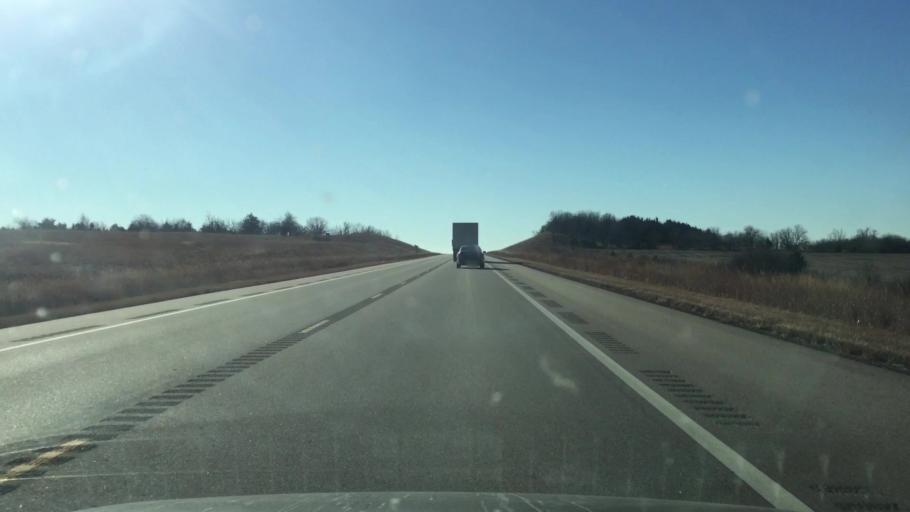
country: US
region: Kansas
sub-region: Allen County
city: Iola
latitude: 38.0161
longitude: -95.3807
